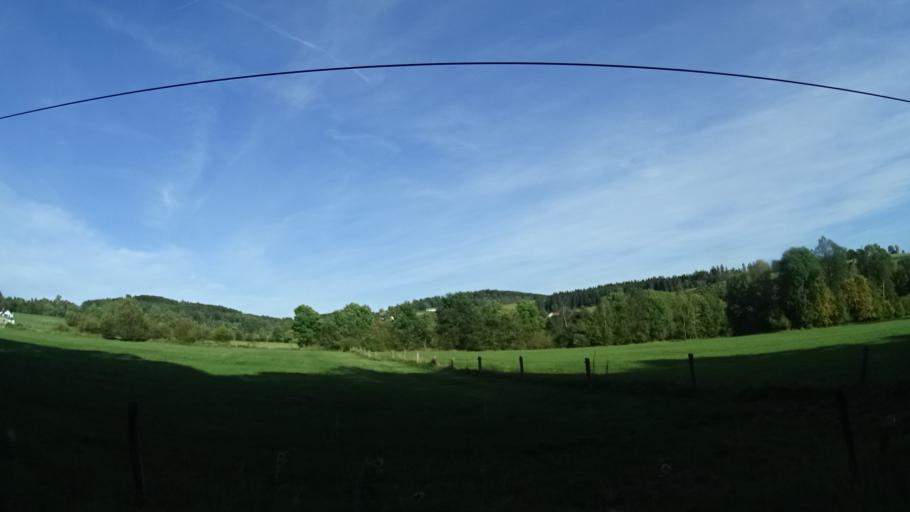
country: DE
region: Hesse
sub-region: Regierungsbezirk Kassel
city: Poppenhausen
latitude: 50.5185
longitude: 9.8687
